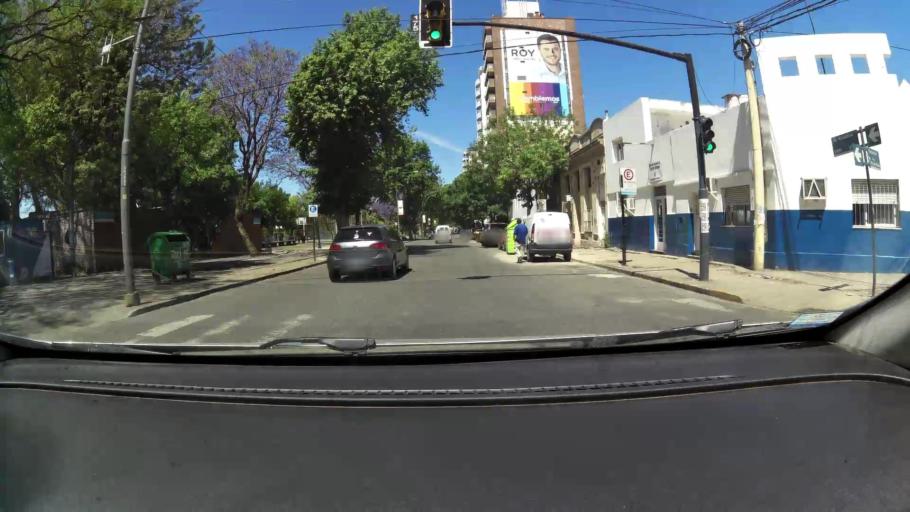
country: AR
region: Santa Fe
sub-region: Departamento de Rosario
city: Rosario
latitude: -32.9314
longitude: -60.6543
